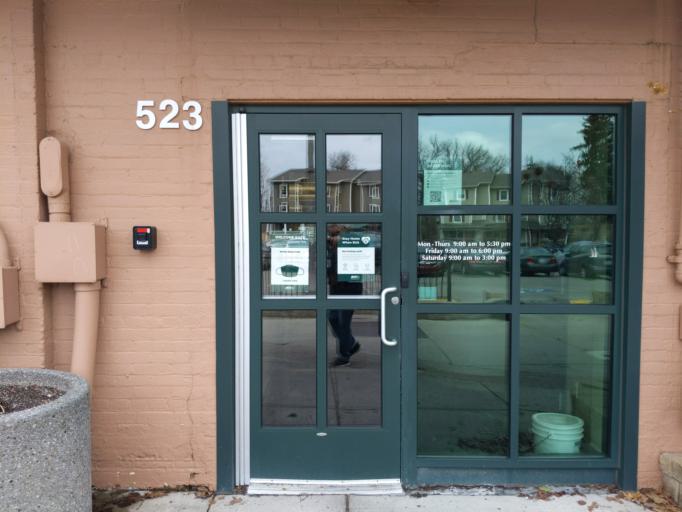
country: US
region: Michigan
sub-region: Ingham County
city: East Lansing
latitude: 42.7340
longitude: -84.4775
